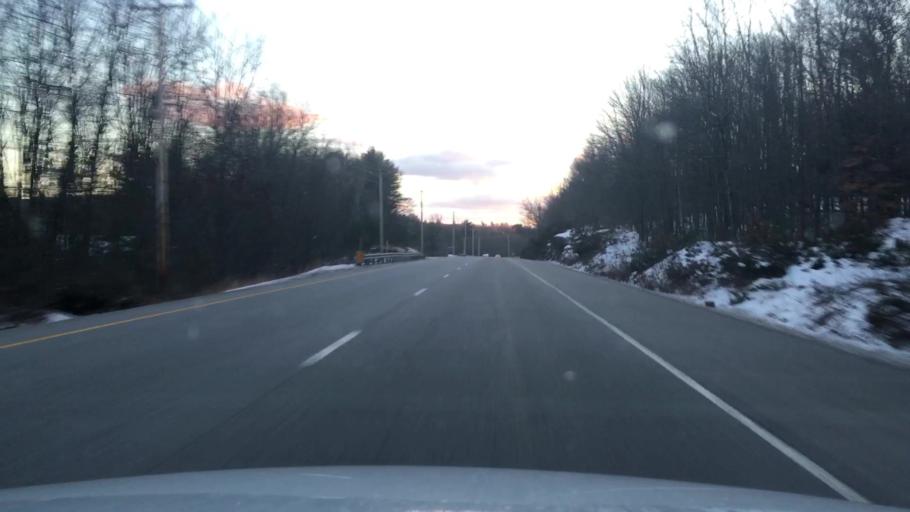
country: US
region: Maine
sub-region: Androscoggin County
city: Auburn
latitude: 44.0520
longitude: -70.2562
